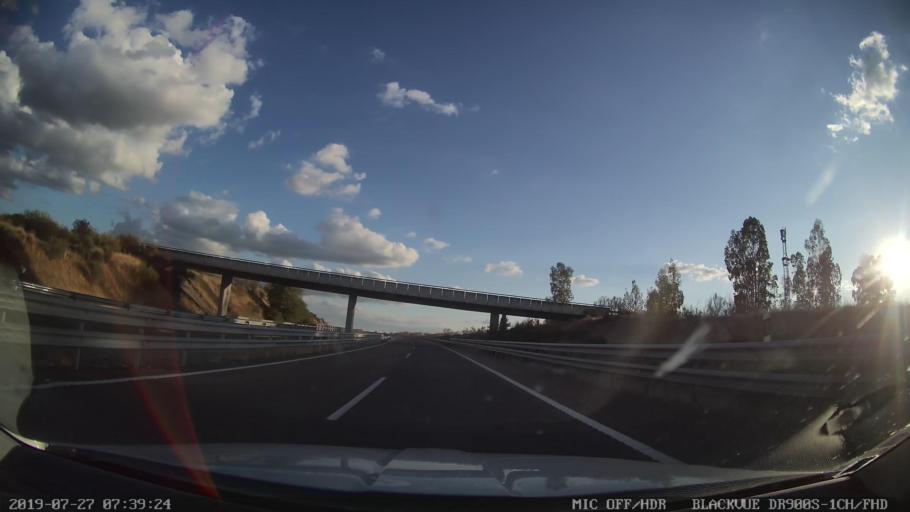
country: ES
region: Extremadura
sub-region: Provincia de Badajoz
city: Santa Amalia
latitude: 39.0644
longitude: -6.0541
